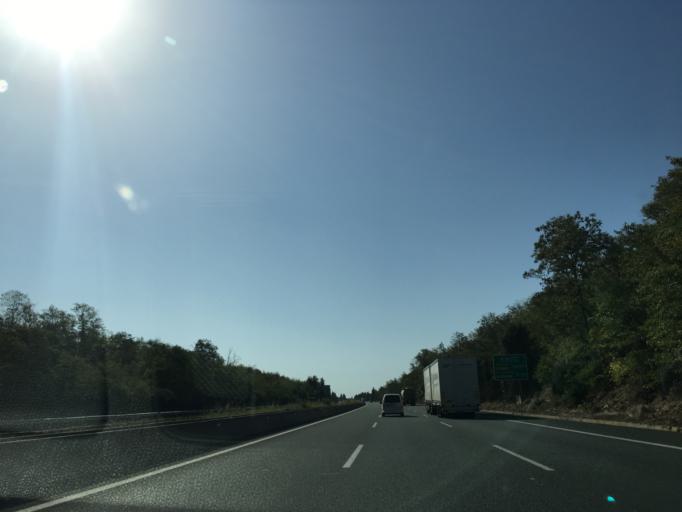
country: GR
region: Central Macedonia
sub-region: Nomos Pierias
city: Makrygialos
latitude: 40.4081
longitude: 22.5943
